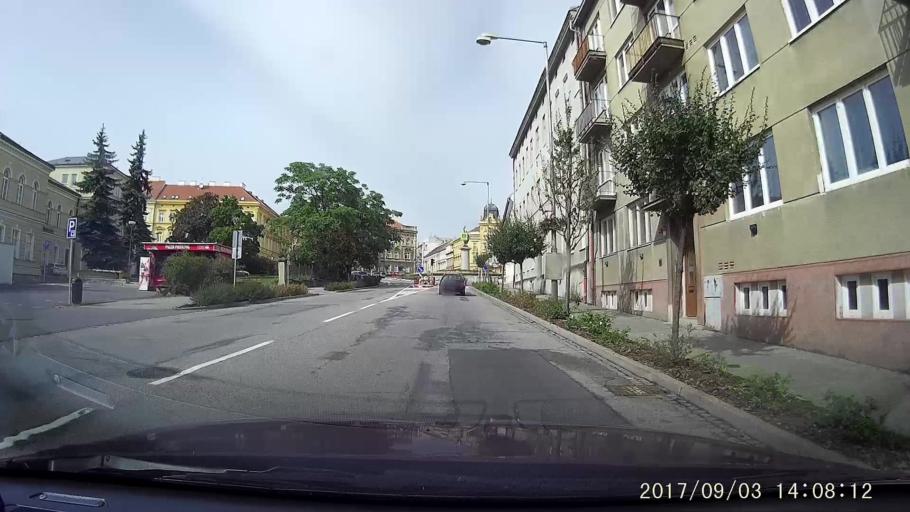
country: CZ
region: South Moravian
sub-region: Okres Znojmo
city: Znojmo
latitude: 48.8549
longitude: 16.0543
